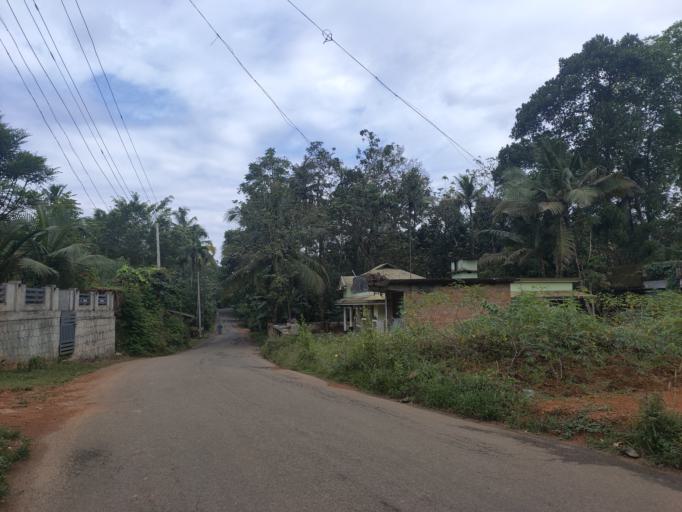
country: IN
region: Kerala
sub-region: Ernakulam
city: Muvattupula
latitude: 9.9946
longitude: 76.6366
